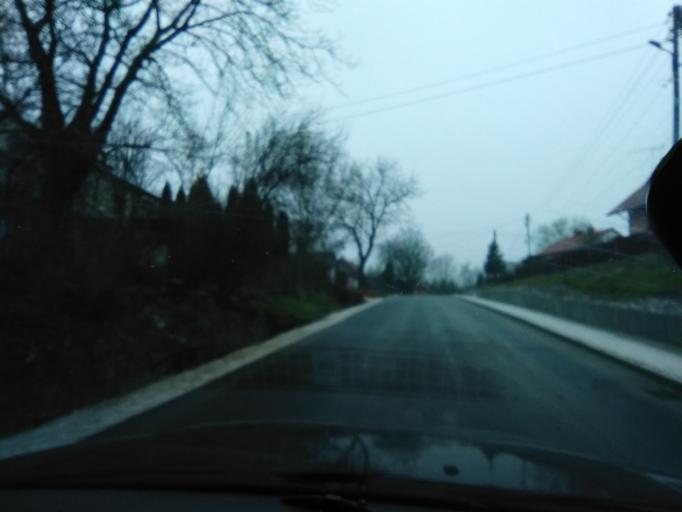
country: PL
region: Subcarpathian Voivodeship
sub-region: Powiat przeworski
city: Gac
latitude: 50.0255
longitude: 22.3867
